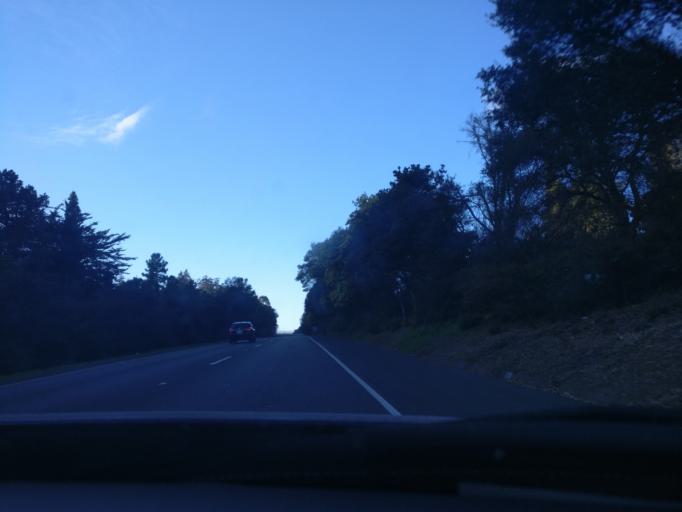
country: US
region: California
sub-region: Alameda County
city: Piedmont
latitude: 37.8234
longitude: -122.2085
